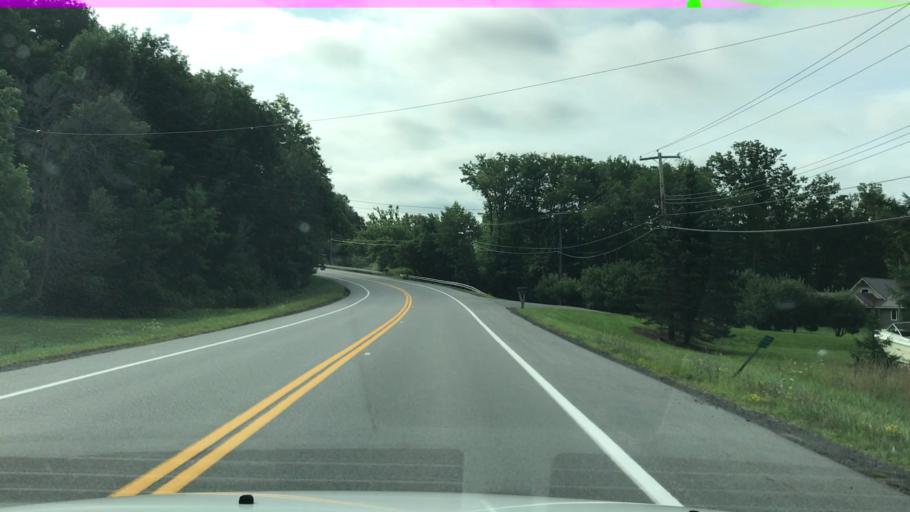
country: US
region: New York
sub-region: Erie County
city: Alden
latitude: 42.8516
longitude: -78.4921
